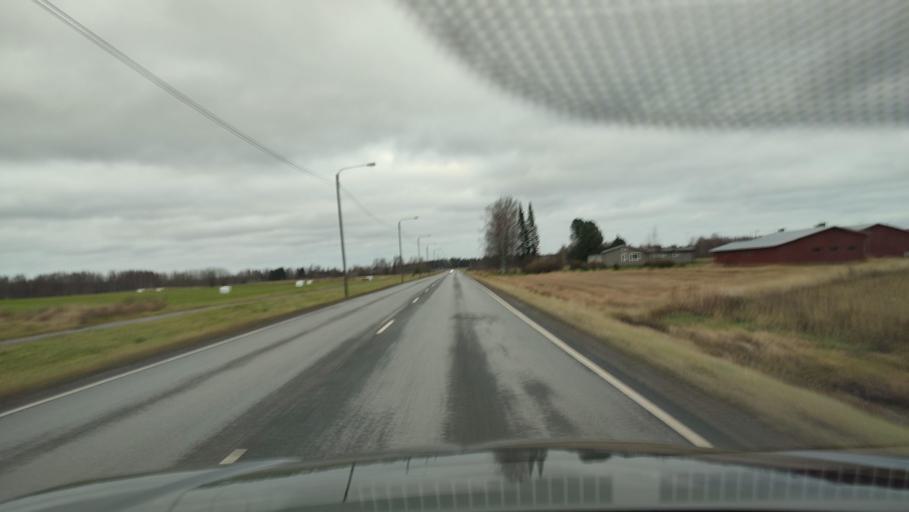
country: FI
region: Southern Ostrobothnia
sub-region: Seinaejoki
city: Kurikka
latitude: 62.6065
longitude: 22.4198
